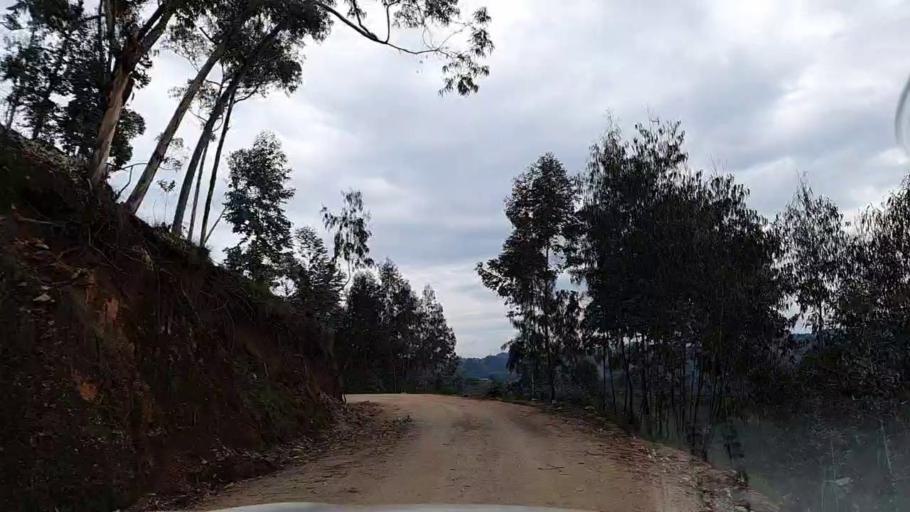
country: RW
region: Southern Province
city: Nzega
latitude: -2.3856
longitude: 29.4503
